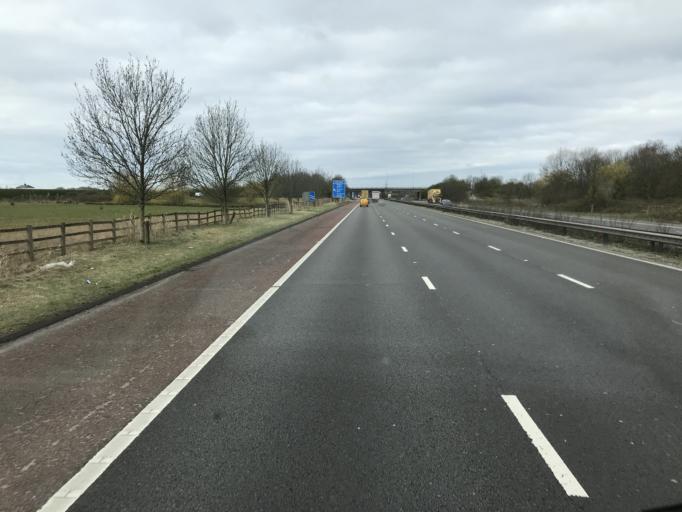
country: GB
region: England
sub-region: St. Helens
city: St Helens
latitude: 53.4066
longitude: -2.7265
